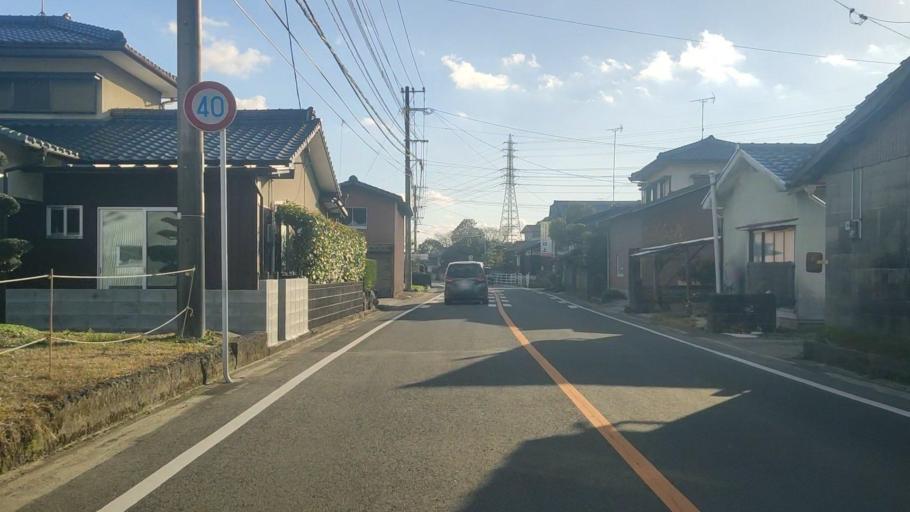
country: JP
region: Saga Prefecture
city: Saga-shi
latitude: 33.3226
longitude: 130.2678
